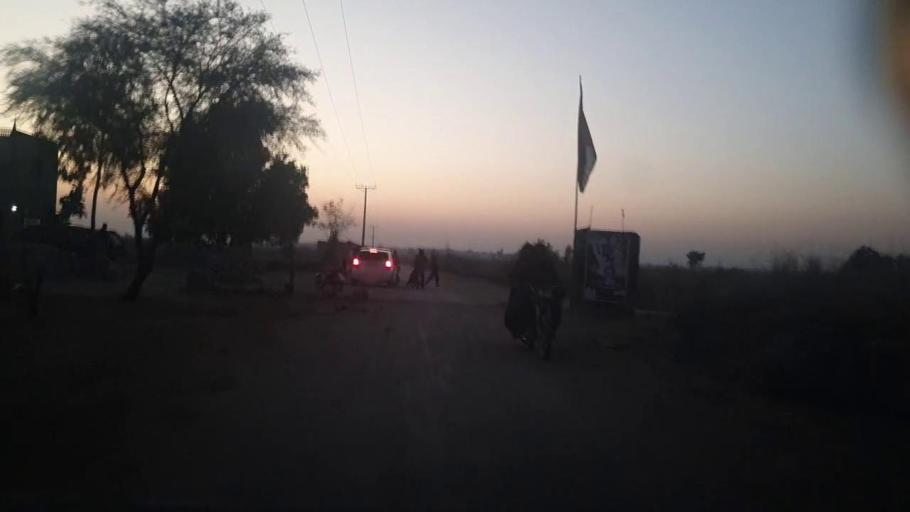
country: PK
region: Sindh
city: Kandiari
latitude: 26.6864
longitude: 68.9161
